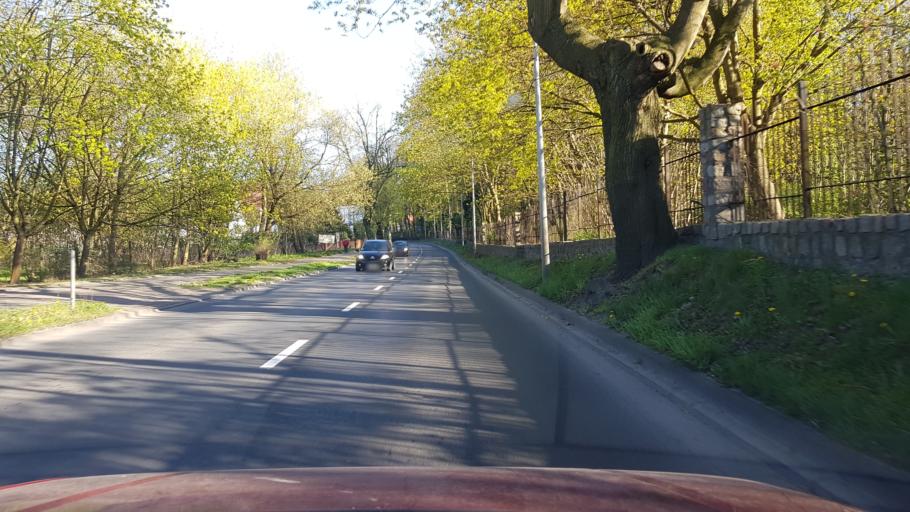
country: PL
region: West Pomeranian Voivodeship
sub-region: Szczecin
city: Szczecin
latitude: 53.3765
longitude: 14.6407
